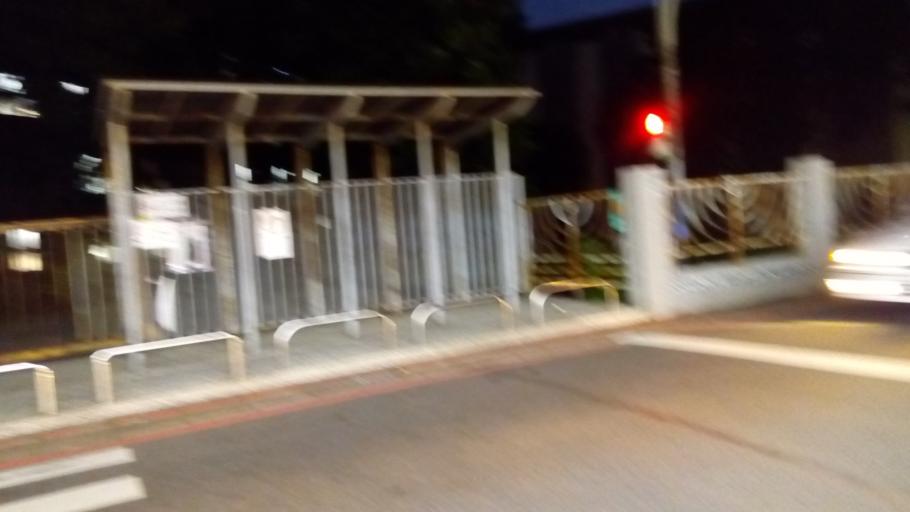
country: TW
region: Taipei
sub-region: Taipei
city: Banqiao
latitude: 25.0346
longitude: 121.4308
